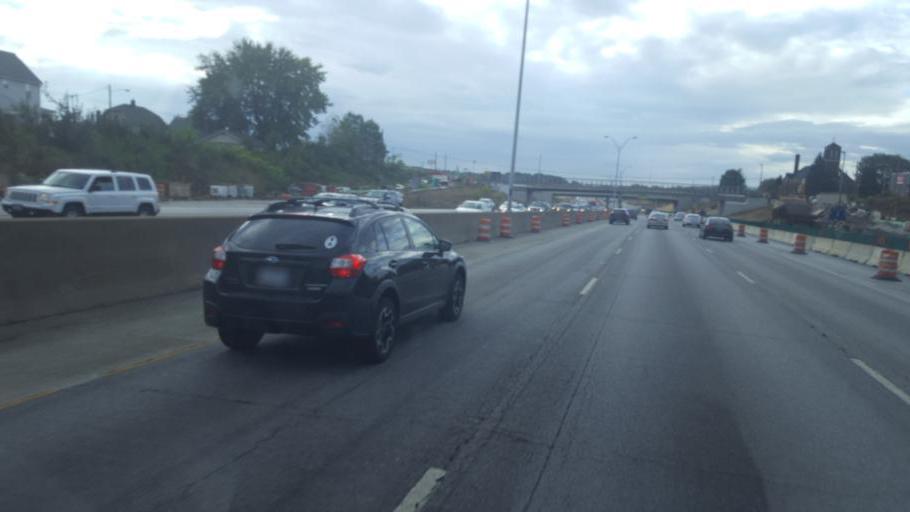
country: US
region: Ohio
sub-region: Summit County
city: Akron
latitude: 41.0626
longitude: -81.5155
